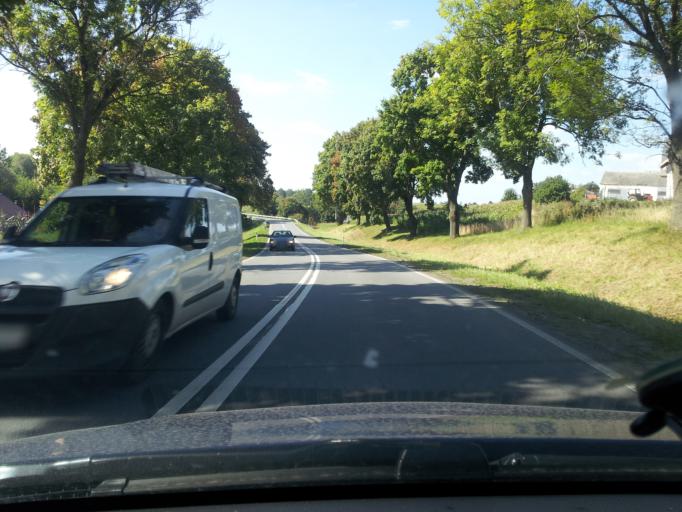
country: PL
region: Kujawsko-Pomorskie
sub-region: Powiat rypinski
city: Ostrowite
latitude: 53.0686
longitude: 19.3151
